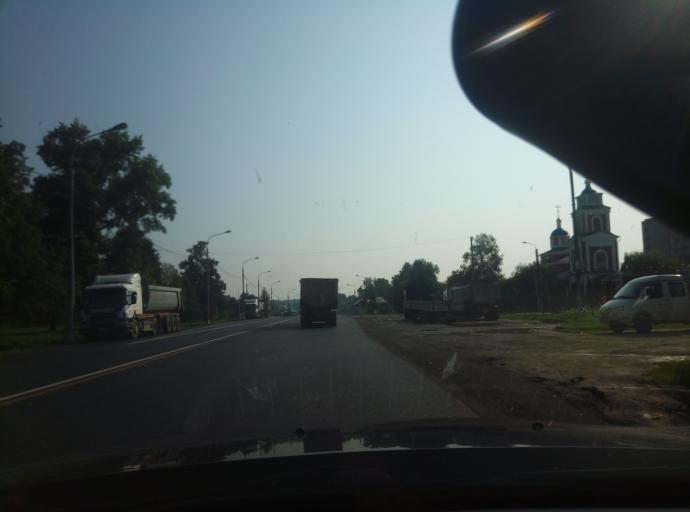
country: RU
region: Kaluga
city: Belousovo
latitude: 55.0908
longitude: 36.6610
